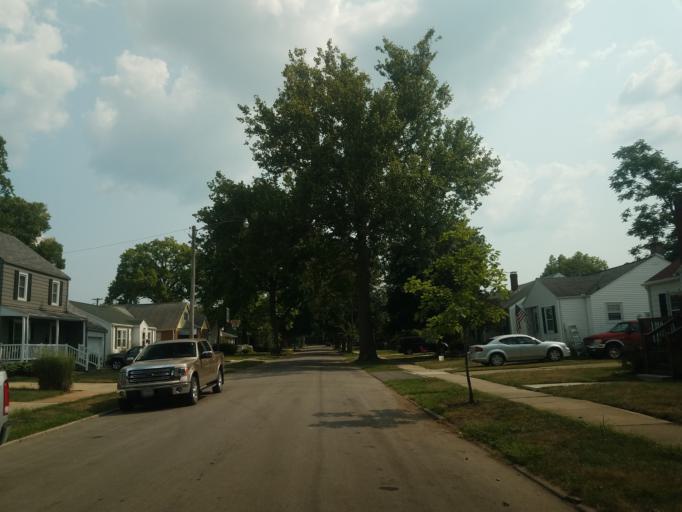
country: US
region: Illinois
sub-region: McLean County
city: Bloomington
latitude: 40.4729
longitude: -88.9707
